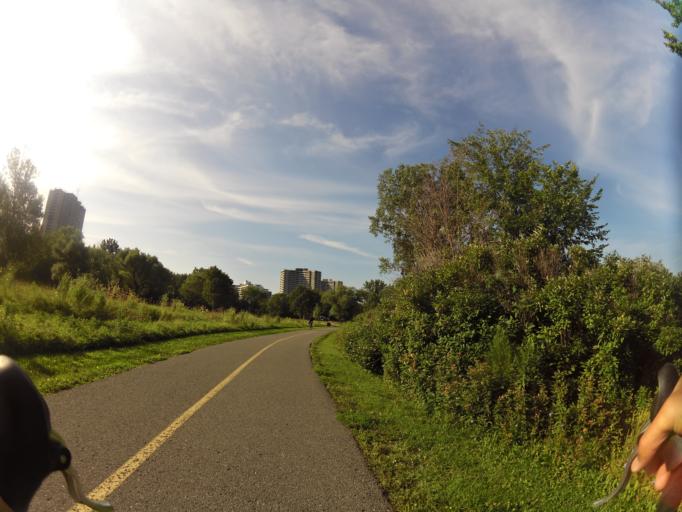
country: CA
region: Ontario
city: Bells Corners
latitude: 45.3779
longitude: -75.7797
